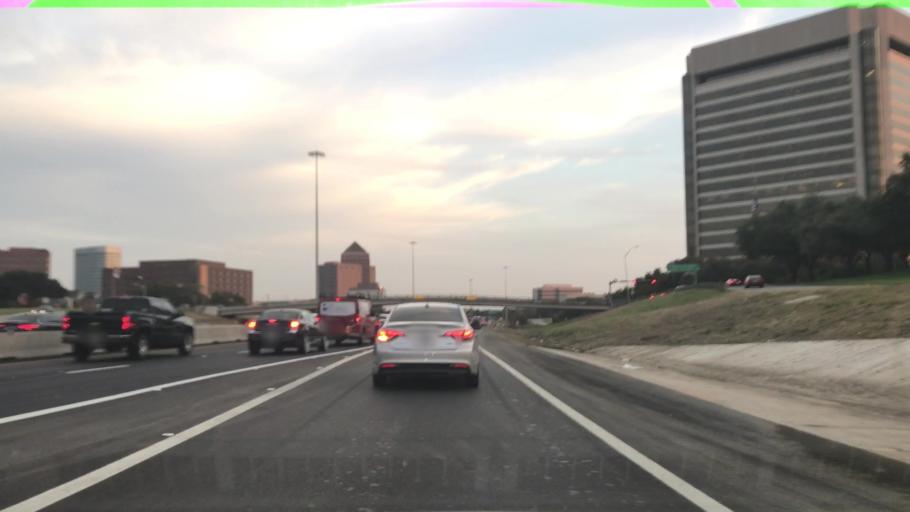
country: US
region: Texas
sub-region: Dallas County
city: Irving
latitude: 32.8649
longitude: -96.9407
